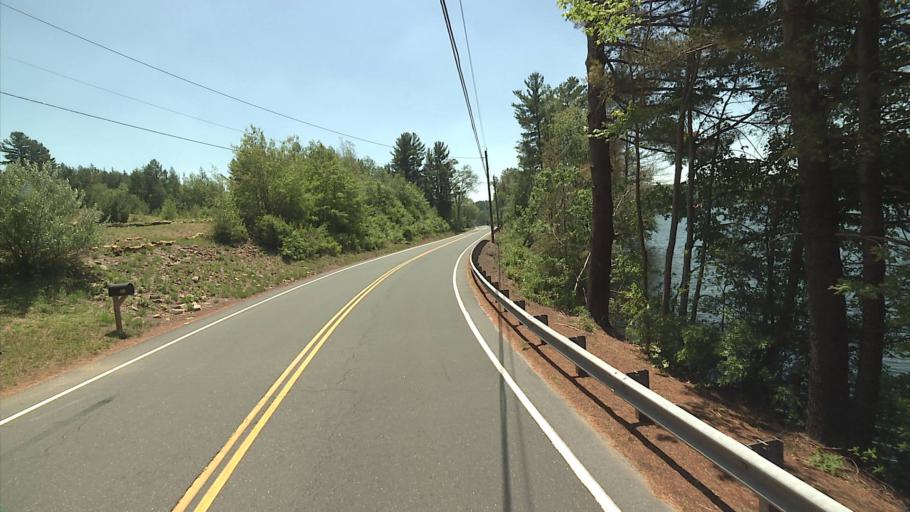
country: US
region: Connecticut
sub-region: Tolland County
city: Stafford
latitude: 42.0002
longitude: -72.2549
